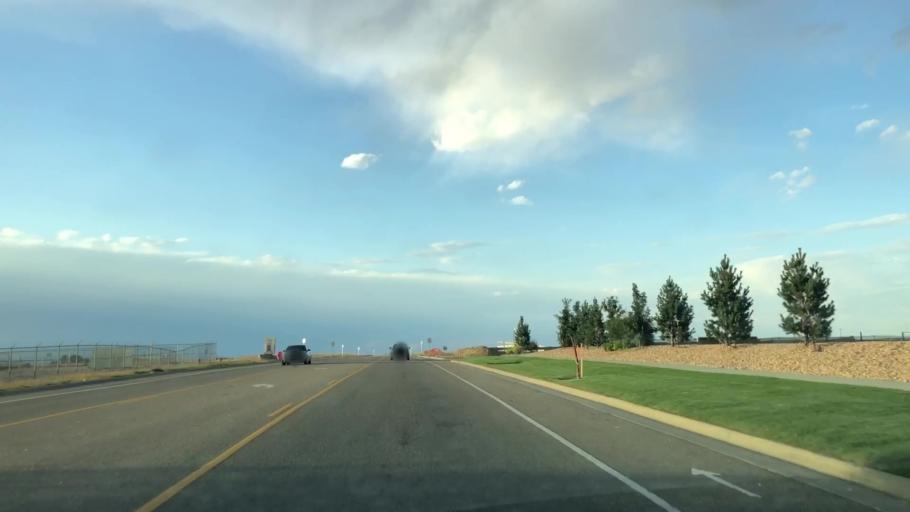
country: US
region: Colorado
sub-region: Larimer County
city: Loveland
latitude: 40.4379
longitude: -104.9958
